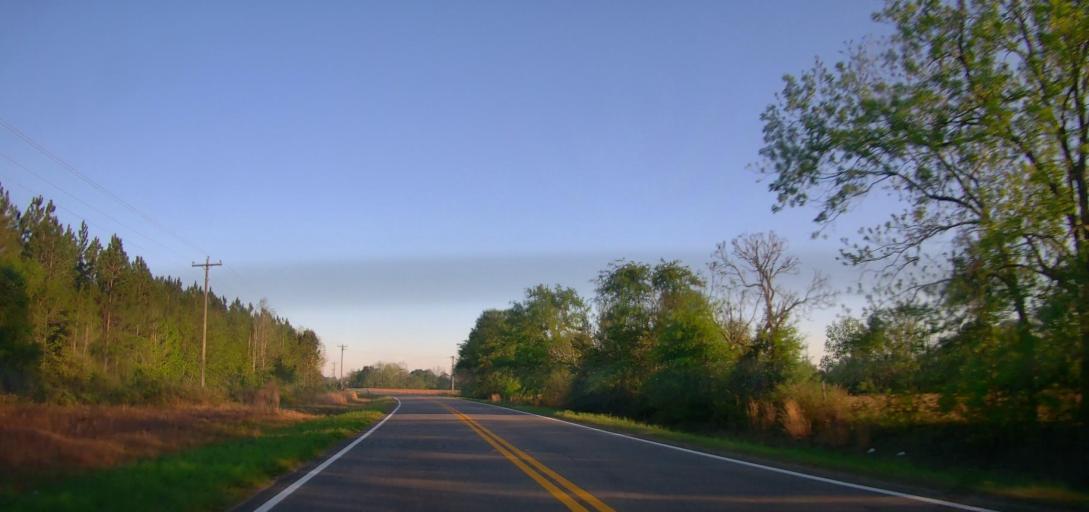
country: US
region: Georgia
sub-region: Irwin County
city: Ocilla
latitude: 31.6143
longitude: -83.2646
